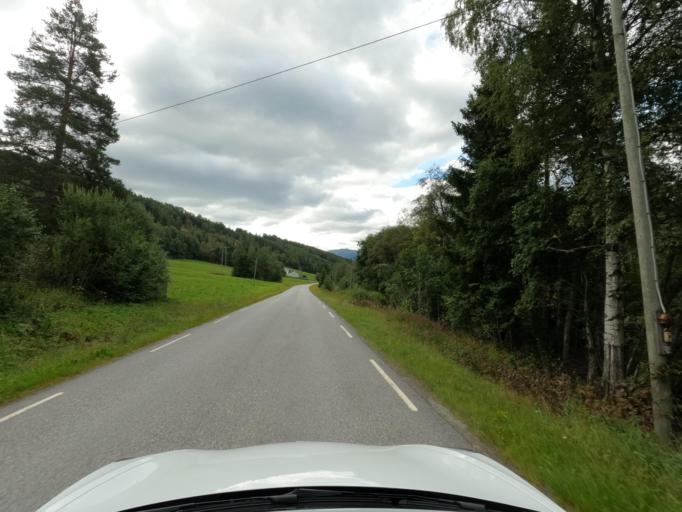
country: NO
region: Buskerud
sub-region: Nore og Uvdal
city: Rodberg
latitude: 60.0159
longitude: 8.8373
